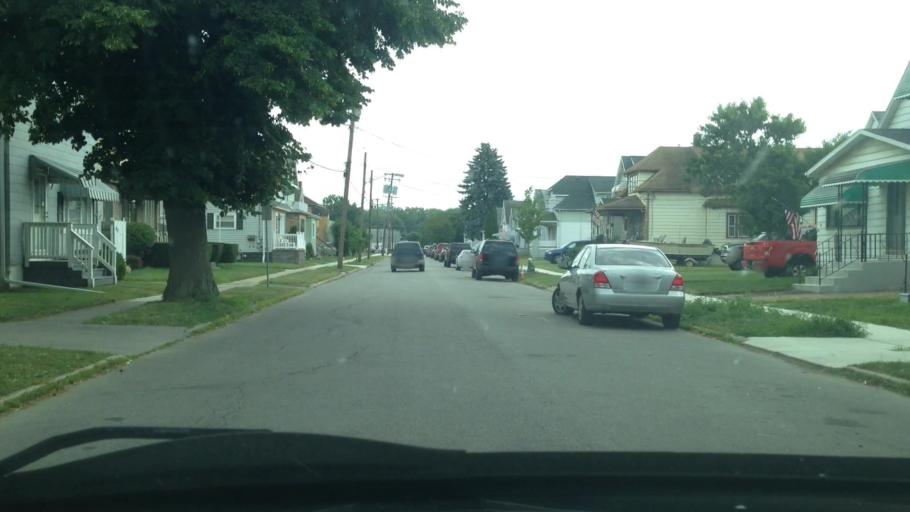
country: US
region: New York
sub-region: Erie County
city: Sloan
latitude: 42.8737
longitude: -78.7969
